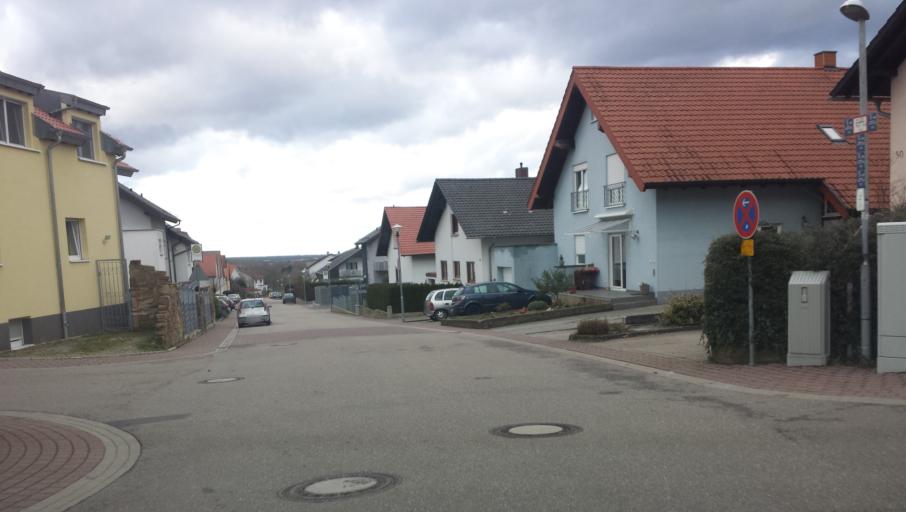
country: DE
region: Baden-Wuerttemberg
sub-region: Karlsruhe Region
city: Malsch
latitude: 49.2566
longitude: 8.6838
